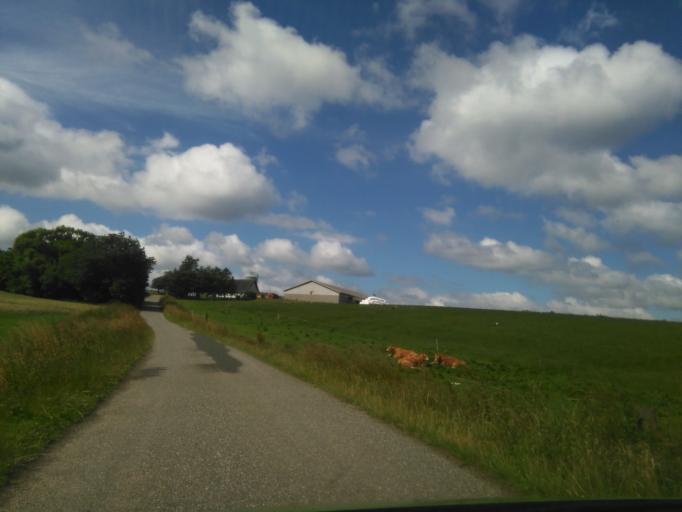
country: DK
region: Central Jutland
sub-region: Syddjurs Kommune
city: Ronde
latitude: 56.2402
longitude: 10.4844
